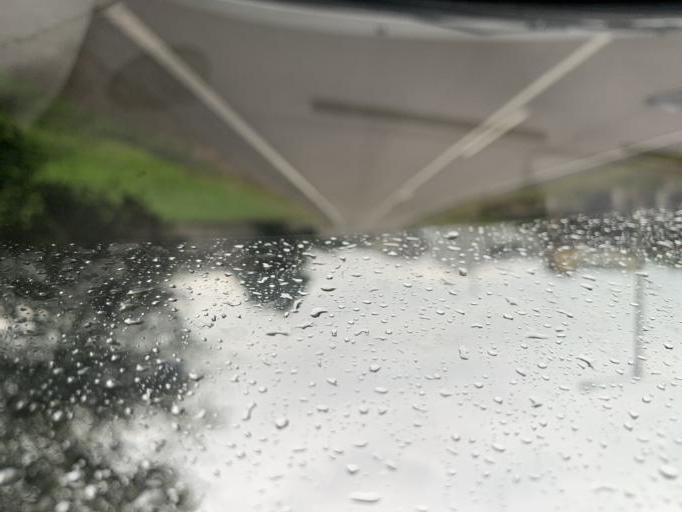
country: ES
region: Galicia
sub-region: Provincia de Lugo
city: Barreiros
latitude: 43.5495
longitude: -7.1426
